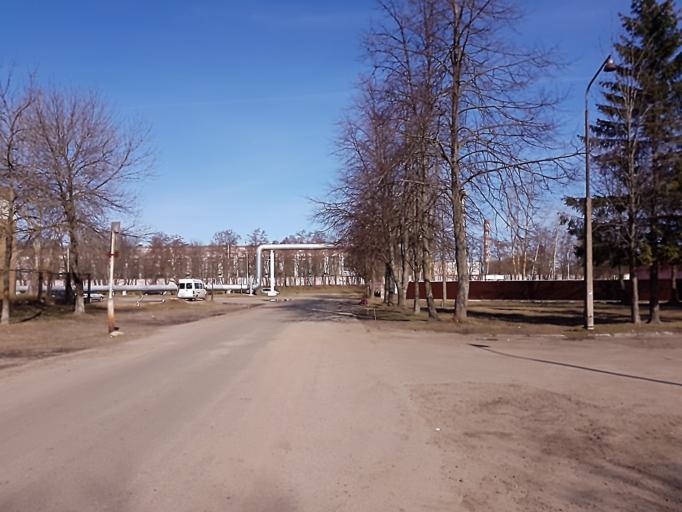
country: BY
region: Mogilev
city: Babruysk
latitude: 53.1802
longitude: 29.2078
